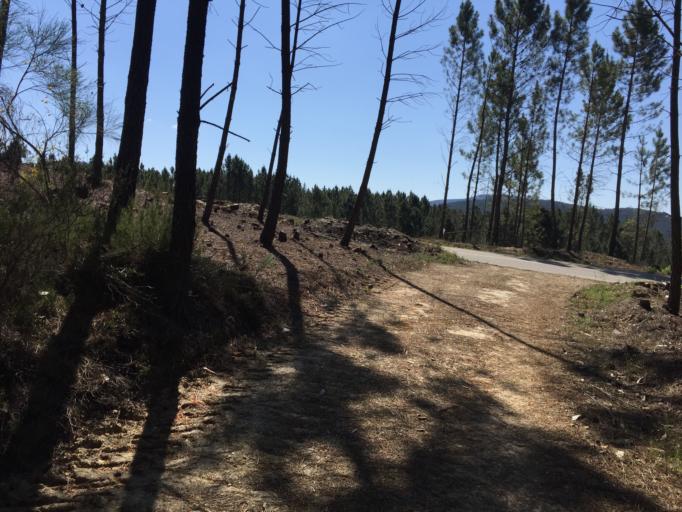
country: PT
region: Coimbra
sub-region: Pampilhosa da Serra
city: Pampilhosa da Serra
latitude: 40.0823
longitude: -7.7795
